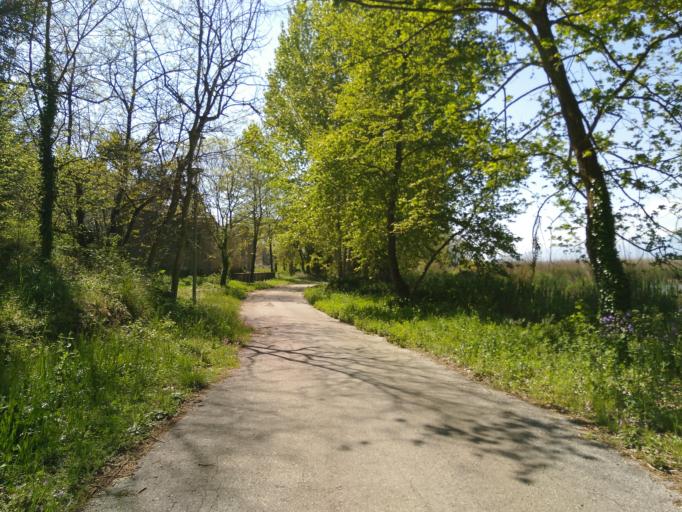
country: GR
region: Epirus
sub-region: Nomos Ioanninon
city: Ioannina
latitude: 39.6776
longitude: 20.8729
